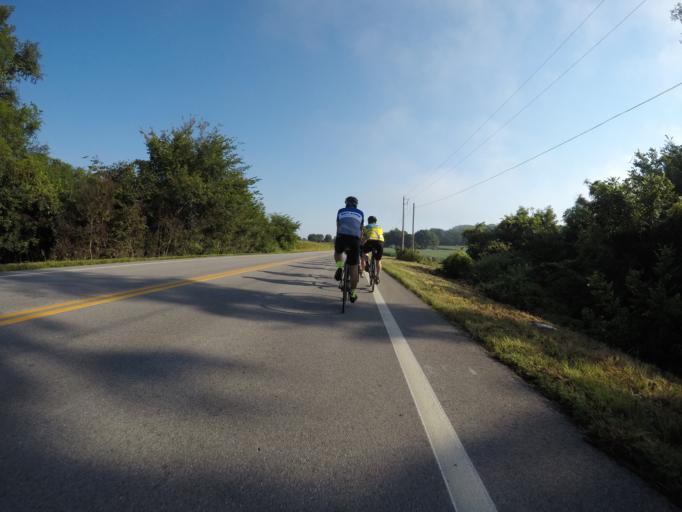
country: US
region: Missouri
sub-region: Platte County
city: Weston
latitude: 39.3721
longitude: -94.8654
